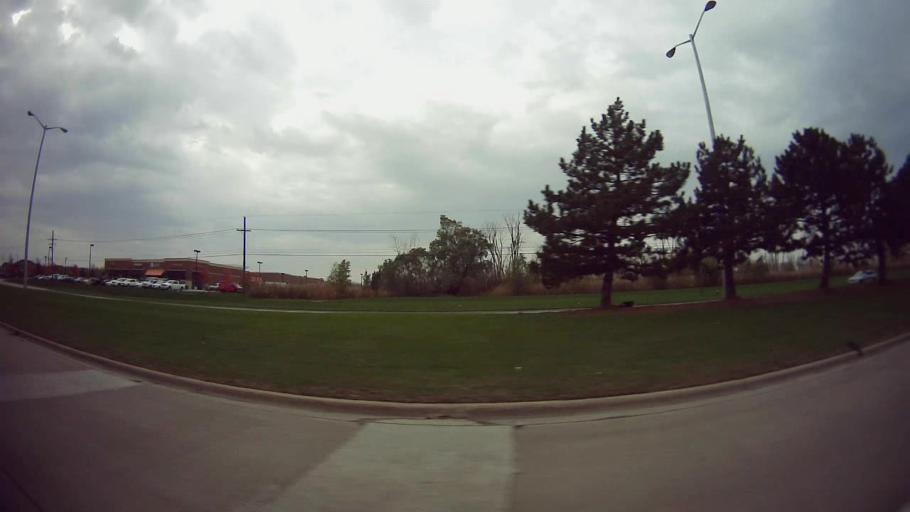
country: US
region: Michigan
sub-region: Macomb County
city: Center Line
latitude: 42.5150
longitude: -83.0466
